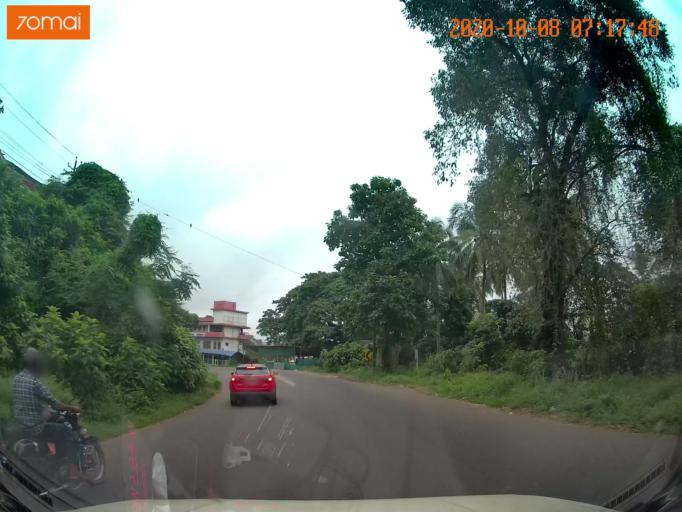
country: IN
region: Kerala
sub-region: Malappuram
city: Ponnani
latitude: 10.8389
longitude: 76.0215
